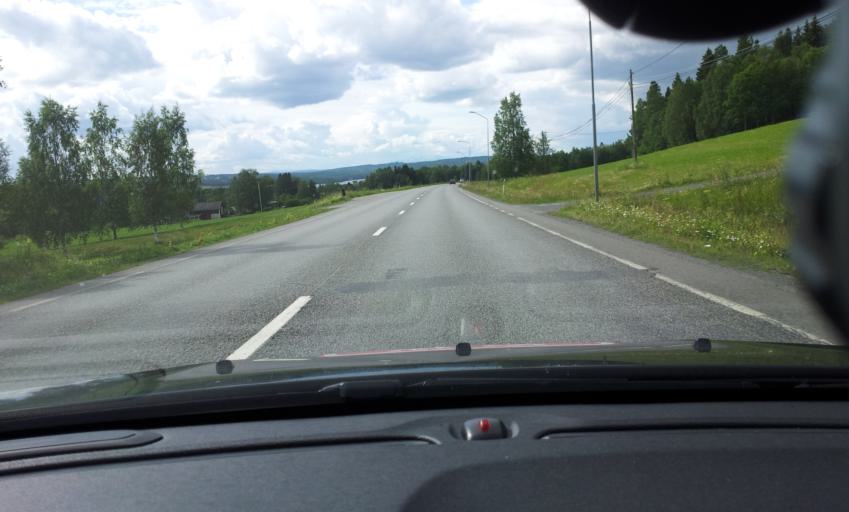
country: SE
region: Jaemtland
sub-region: Krokoms Kommun
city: Valla
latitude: 63.3192
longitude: 14.0761
